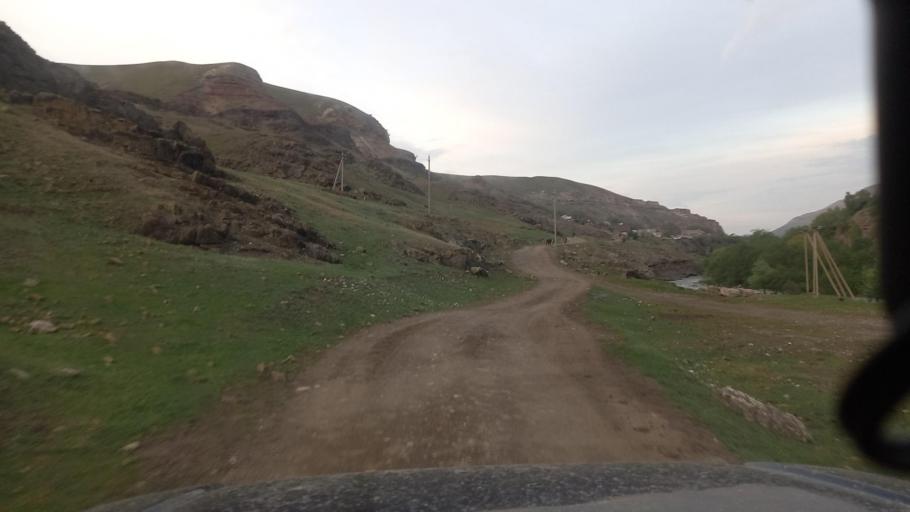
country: RU
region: Kabardino-Balkariya
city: Kamennomostskoye
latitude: 43.7241
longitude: 42.9066
